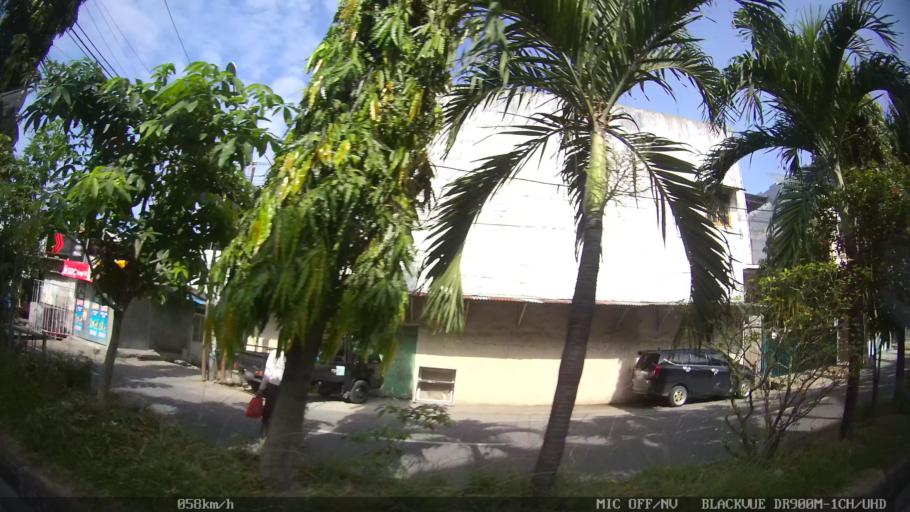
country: ID
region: North Sumatra
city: Medan
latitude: 3.5930
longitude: 98.6615
